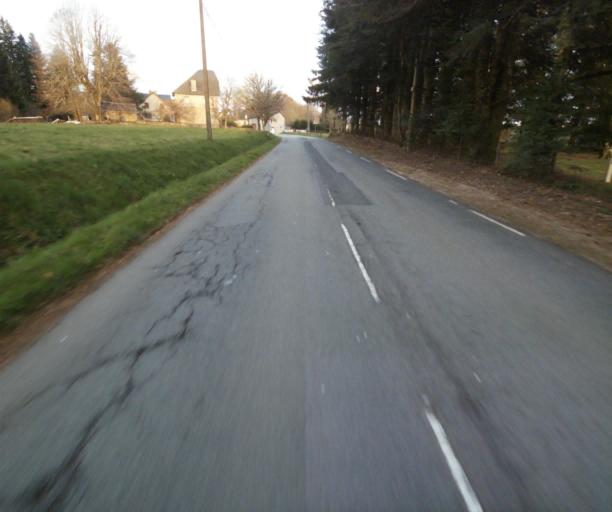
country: FR
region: Limousin
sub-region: Departement de la Correze
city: Correze
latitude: 45.2786
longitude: 1.9661
